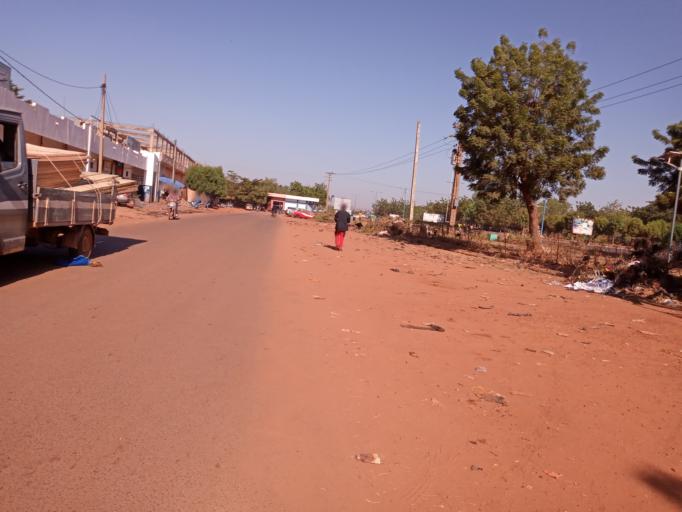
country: ML
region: Bamako
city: Bamako
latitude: 12.5982
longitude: -7.9618
